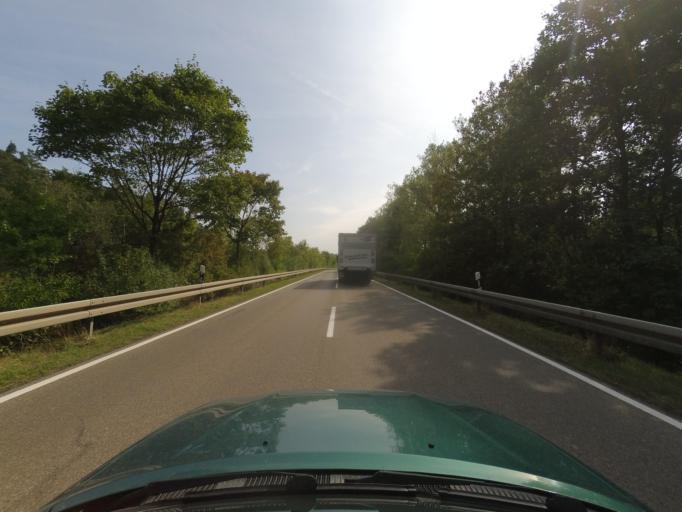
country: DE
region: Bavaria
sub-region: Regierungsbezirk Mittelfranken
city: Feuchtwangen
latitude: 49.1737
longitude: 10.2878
